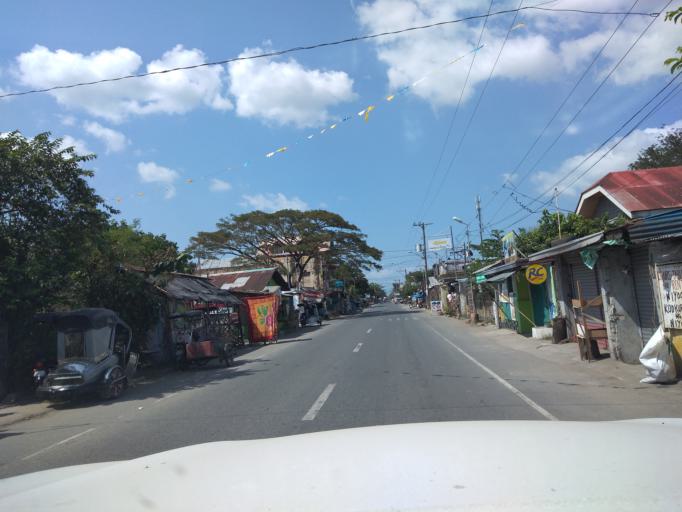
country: PH
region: Central Luzon
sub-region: Province of Pampanga
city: Bahay Pare
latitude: 15.0332
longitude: 120.8812
